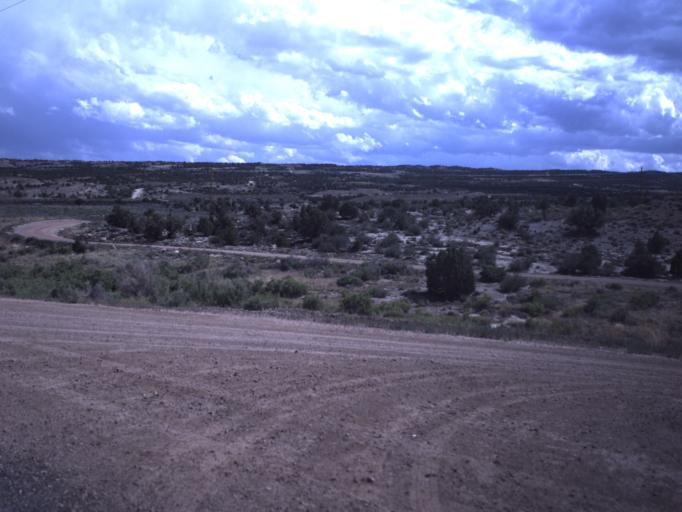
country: US
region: Utah
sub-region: Duchesne County
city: Duchesne
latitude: 40.1746
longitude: -110.4421
